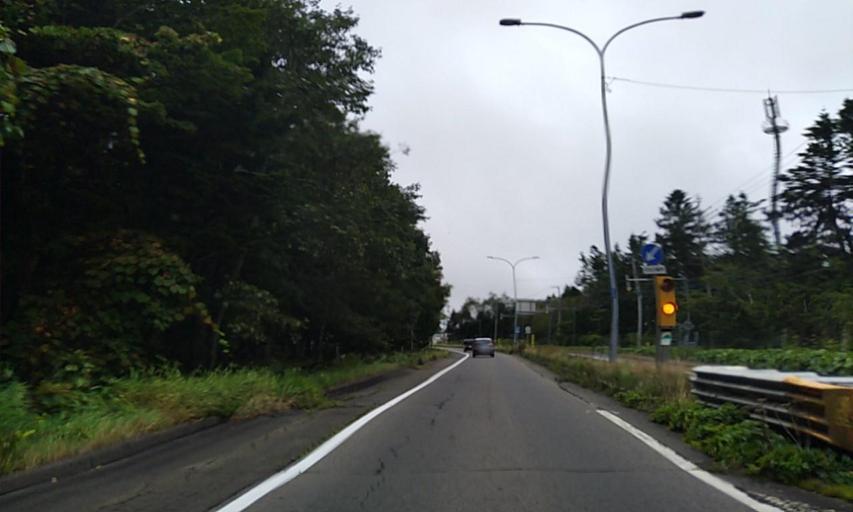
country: JP
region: Hokkaido
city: Nemuro
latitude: 43.2585
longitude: 145.4450
